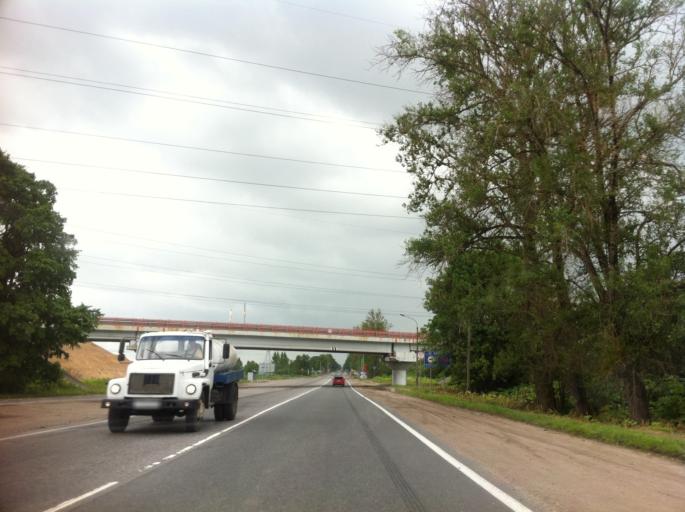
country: RU
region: Leningrad
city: Mariyenburg
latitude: 59.5208
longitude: 30.0670
